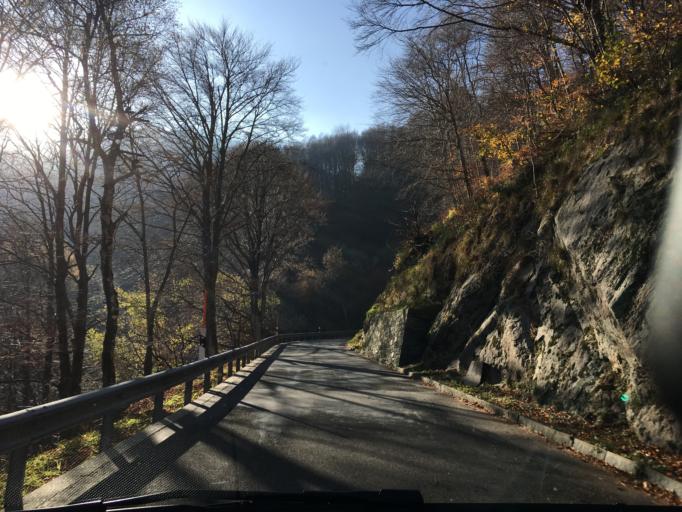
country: CH
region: Ticino
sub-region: Locarno District
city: Magadino
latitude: 46.1170
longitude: 8.8476
